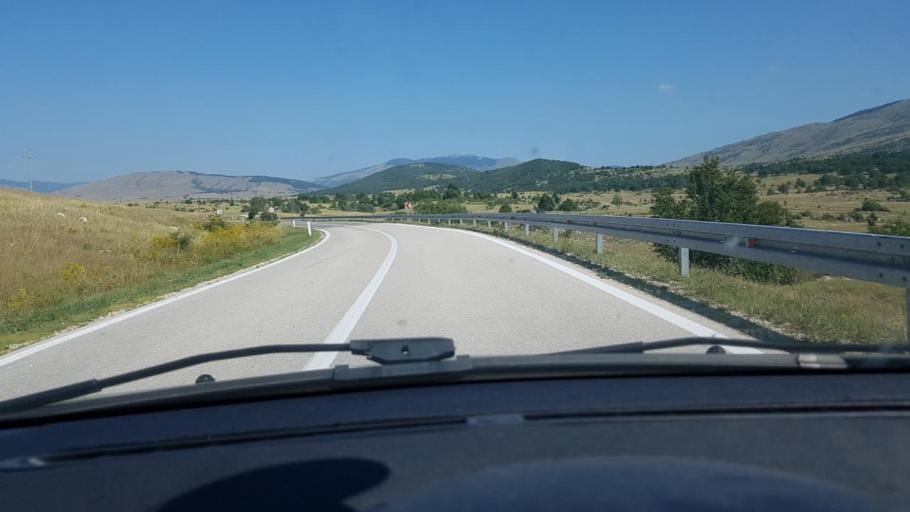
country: BA
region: Federation of Bosnia and Herzegovina
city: Bosansko Grahovo
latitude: 44.1362
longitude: 16.4760
